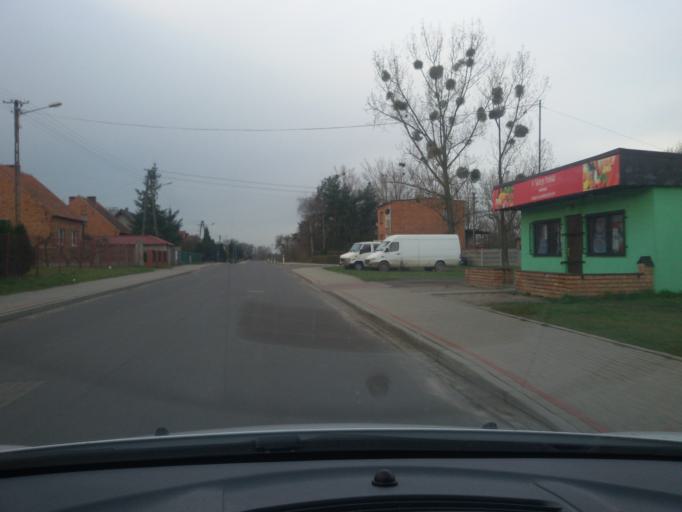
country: PL
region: Greater Poland Voivodeship
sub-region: Powiat gostynski
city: Krobia
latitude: 51.7699
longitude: 16.9315
